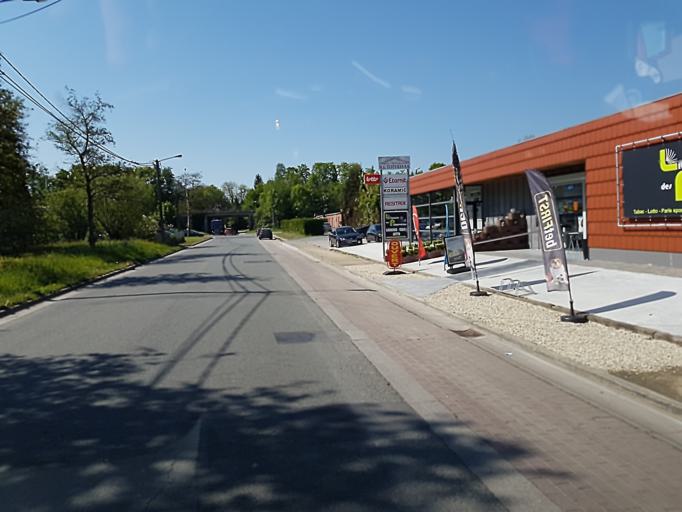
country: BE
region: Wallonia
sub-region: Province du Hainaut
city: Ath
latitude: 50.6405
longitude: 3.7792
